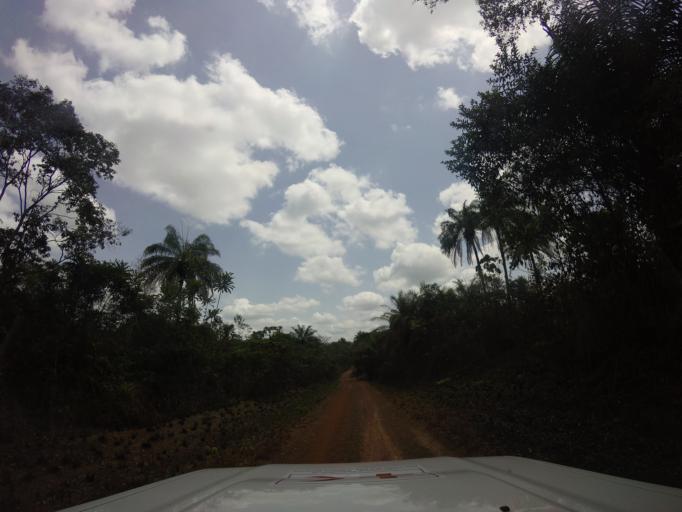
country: SL
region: Southern Province
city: Zimmi
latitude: 7.1961
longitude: -11.2194
